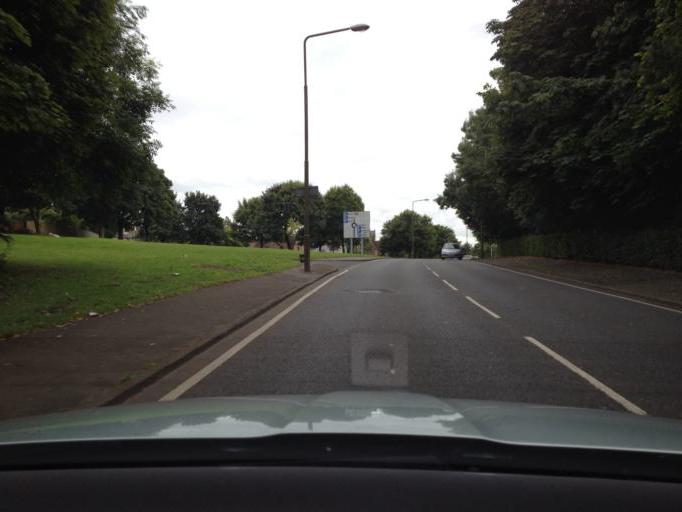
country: GB
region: Scotland
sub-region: West Lothian
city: Bathgate
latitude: 55.9084
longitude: -3.6370
